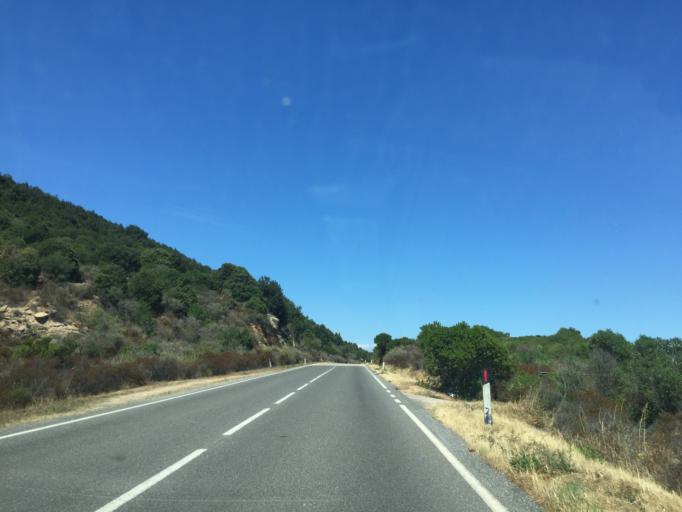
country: IT
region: Sardinia
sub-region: Provincia di Olbia-Tempio
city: Aglientu
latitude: 41.0820
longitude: 9.1167
